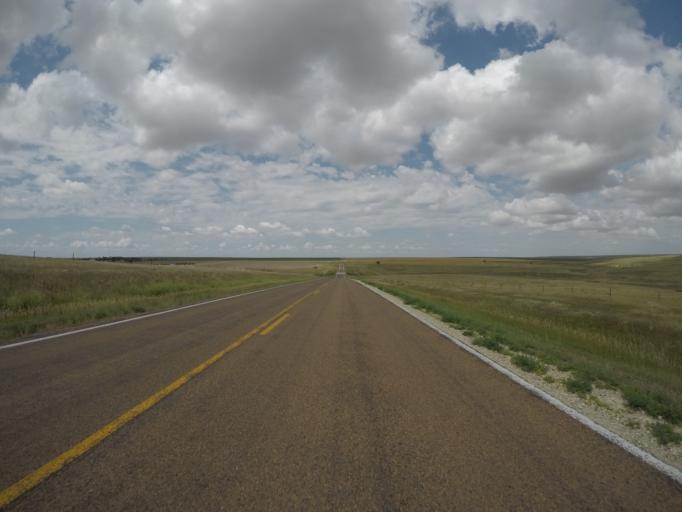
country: US
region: Kansas
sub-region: Rawlins County
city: Atwood
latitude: 39.9209
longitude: -101.0562
